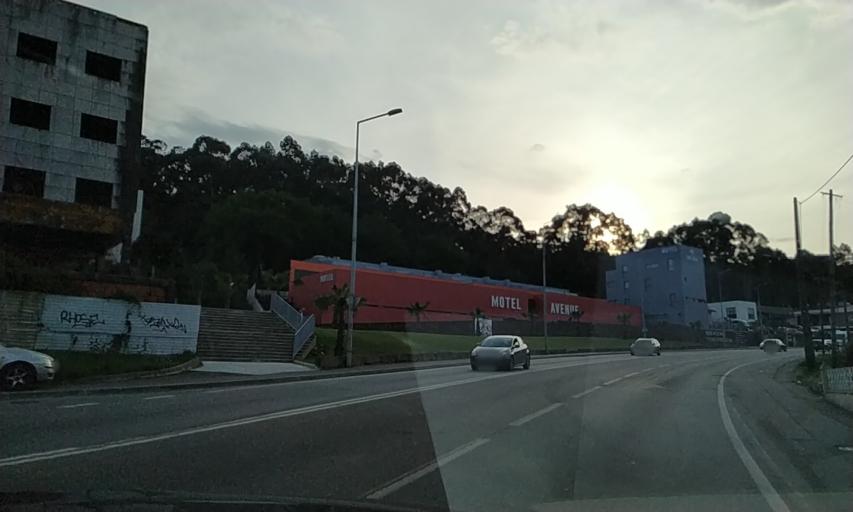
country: PT
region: Porto
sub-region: Valongo
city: Valongo
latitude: 41.1910
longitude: -8.5112
